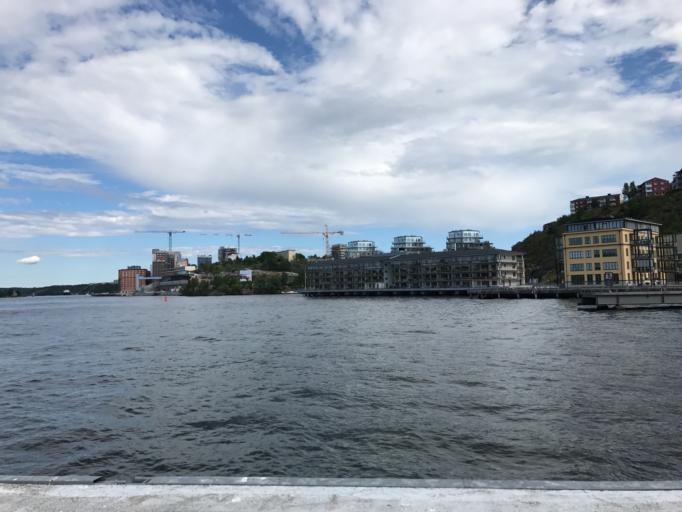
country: SE
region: Stockholm
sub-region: Nacka Kommun
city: Nacka
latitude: 59.3169
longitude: 18.1235
